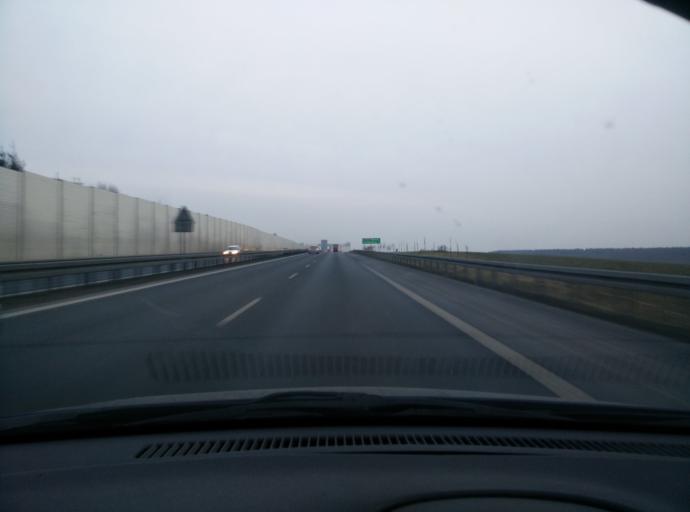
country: PL
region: Greater Poland Voivodeship
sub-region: Powiat poznanski
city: Daszewice
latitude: 52.3171
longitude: 17.0403
